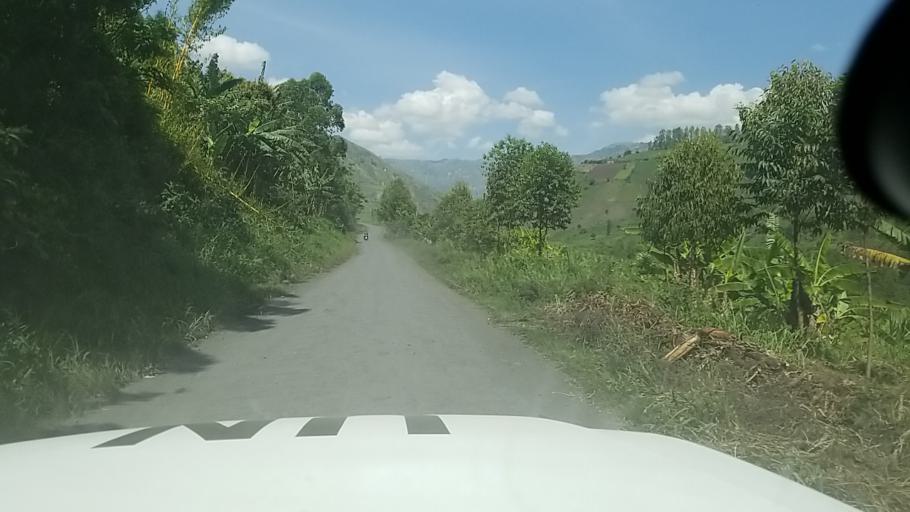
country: CD
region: Nord Kivu
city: Sake
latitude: -1.7390
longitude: 29.0019
